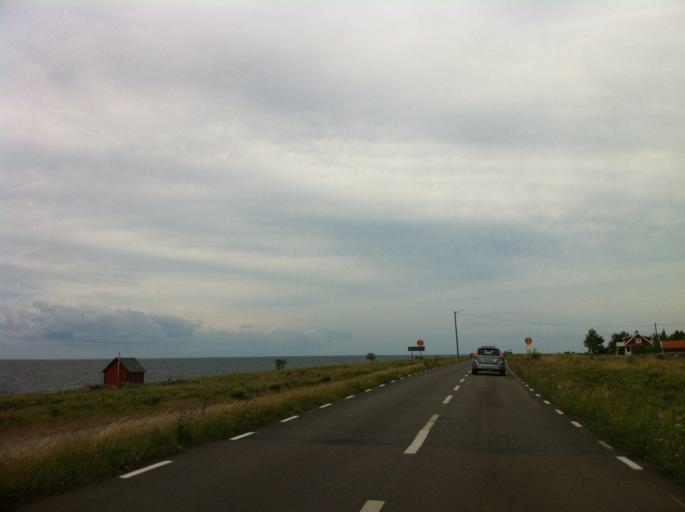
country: SE
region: Kalmar
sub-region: Oskarshamns Kommun
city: Oskarshamn
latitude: 57.3311
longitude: 17.0086
